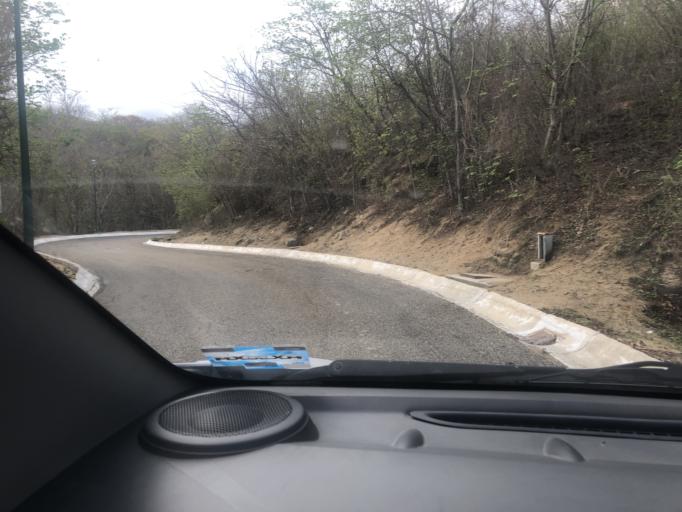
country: MX
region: Oaxaca
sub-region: Santa Maria Huatulco
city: Crucecita
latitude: 15.7730
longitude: -96.0887
